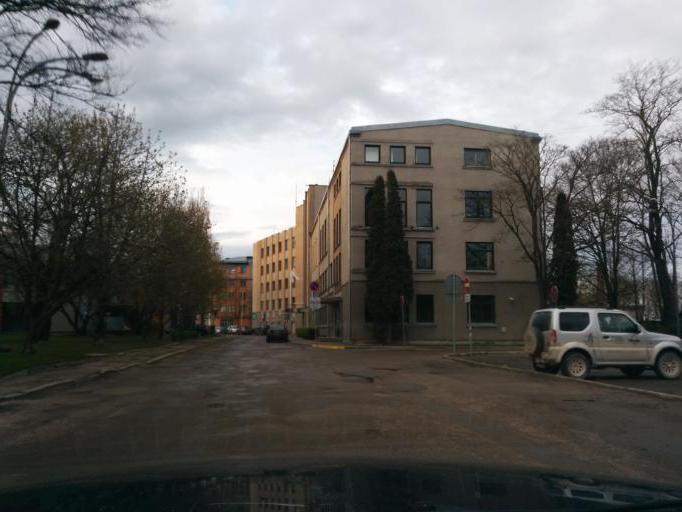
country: LV
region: Jelgava
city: Jelgava
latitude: 56.6479
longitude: 23.7320
